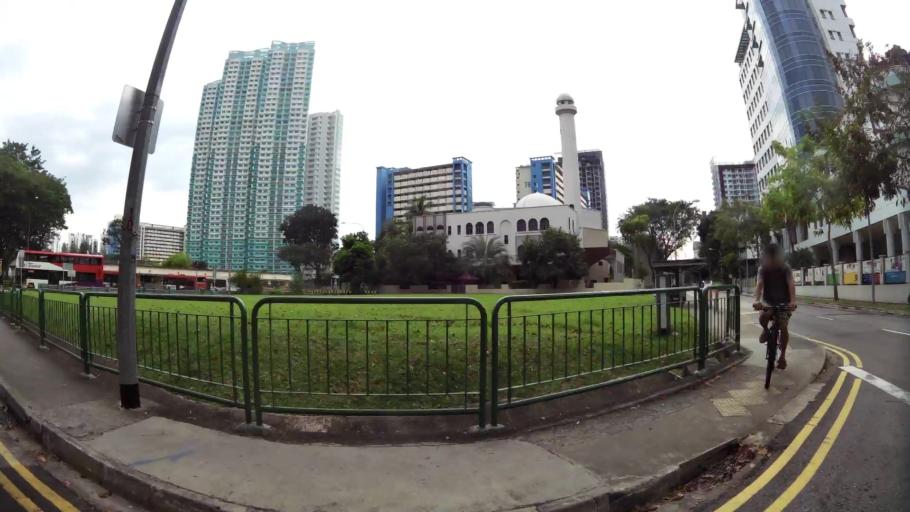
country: SG
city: Singapore
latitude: 1.3268
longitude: 103.8551
